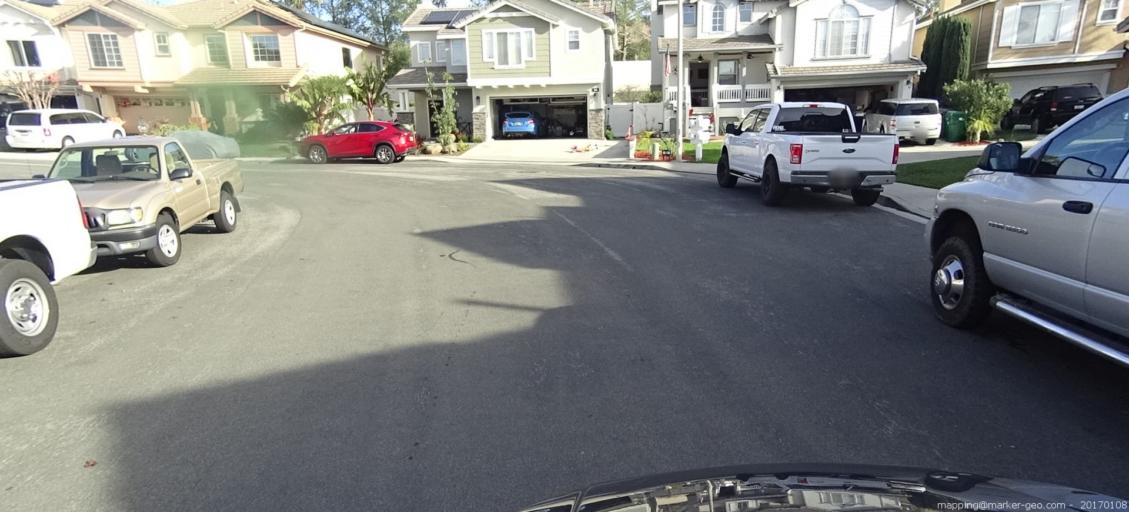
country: US
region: California
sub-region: Orange County
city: Coto De Caza
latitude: 33.5943
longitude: -117.5940
